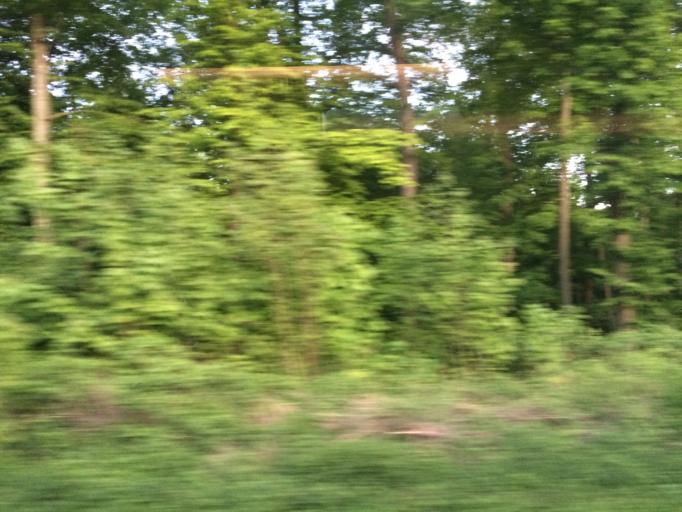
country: DE
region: Bavaria
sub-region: Regierungsbezirk Unterfranken
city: Heigenbrucken
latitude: 50.0172
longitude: 9.3502
